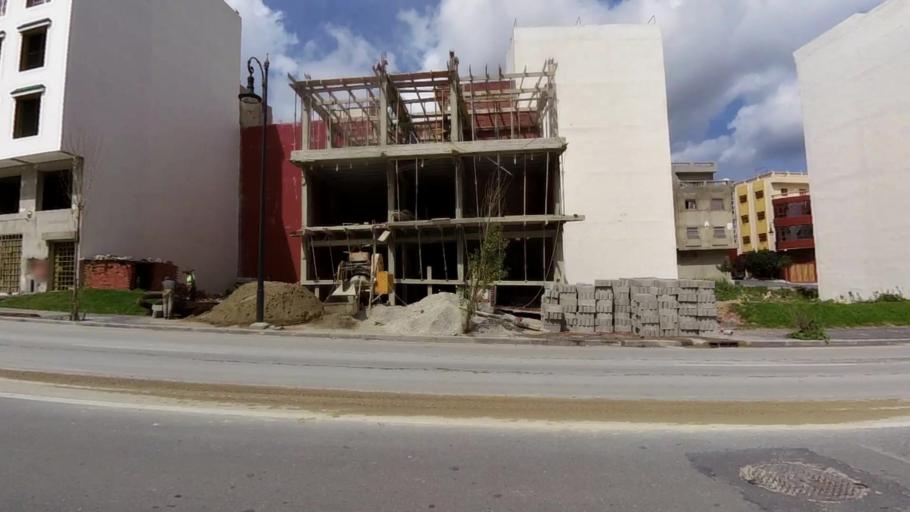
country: MA
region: Tanger-Tetouan
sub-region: Tanger-Assilah
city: Tangier
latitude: 35.7616
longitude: -5.7555
